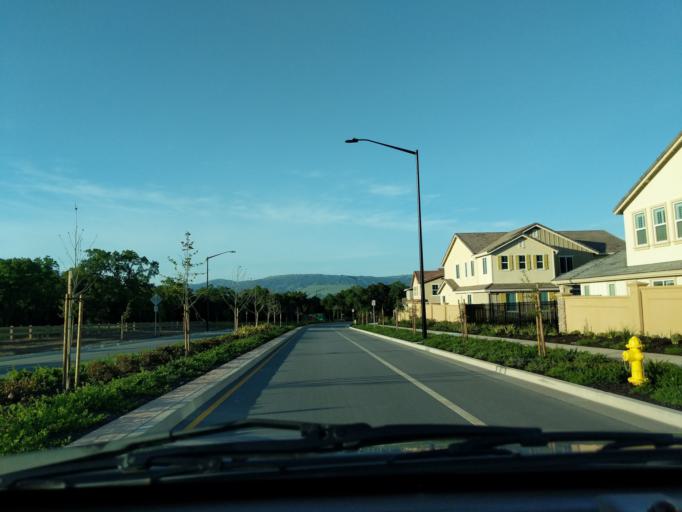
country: US
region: California
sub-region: Santa Clara County
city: Gilroy
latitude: 36.9925
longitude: -121.5832
